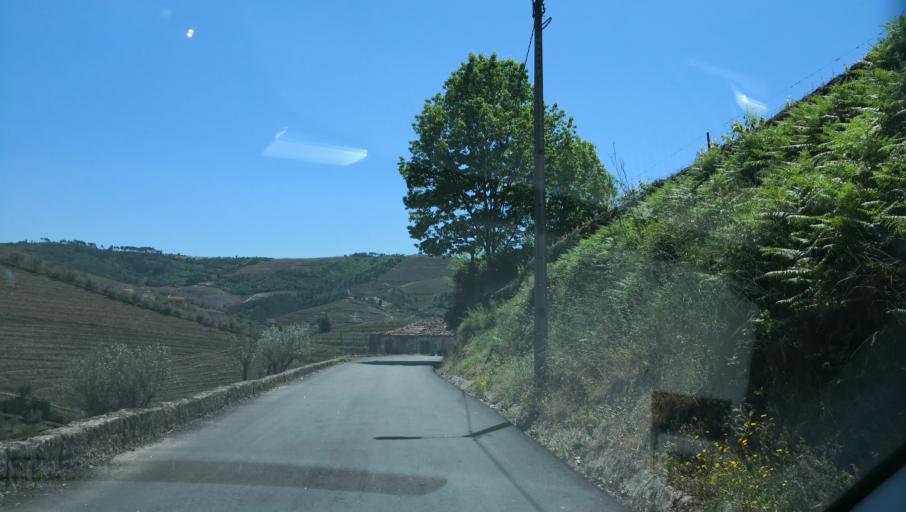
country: PT
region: Vila Real
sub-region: Vila Real
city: Vila Real
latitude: 41.2246
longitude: -7.7203
